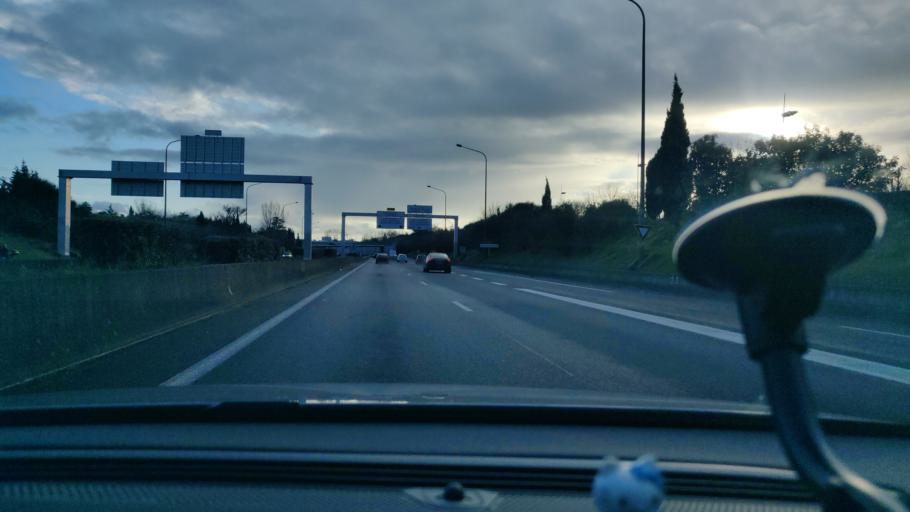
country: FR
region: Midi-Pyrenees
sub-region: Departement de la Haute-Garonne
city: Colomiers
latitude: 43.5952
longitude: 1.3624
